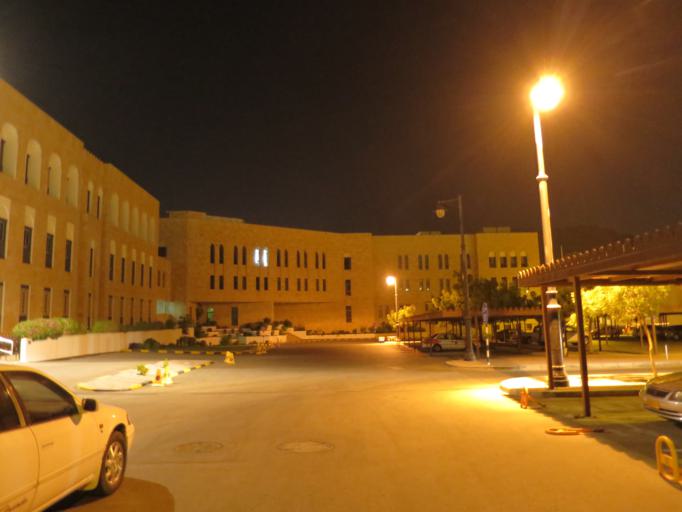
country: OM
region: Muhafazat Masqat
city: Muscat
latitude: 23.6137
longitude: 58.5951
